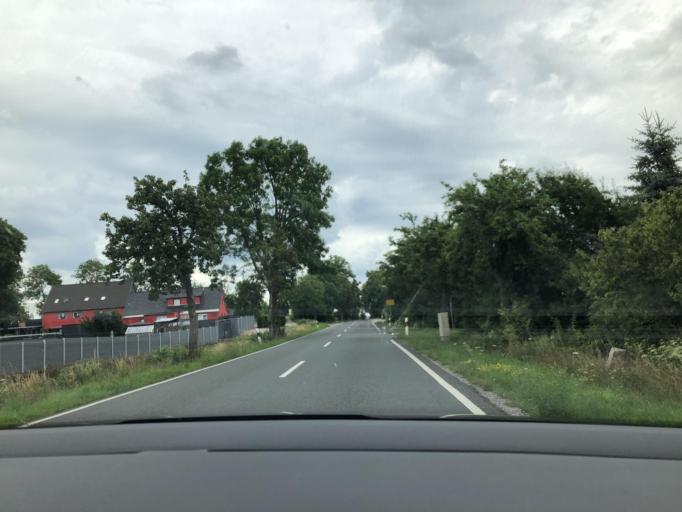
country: DE
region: Saxony-Anhalt
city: Borne
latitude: 51.9447
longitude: 11.5513
